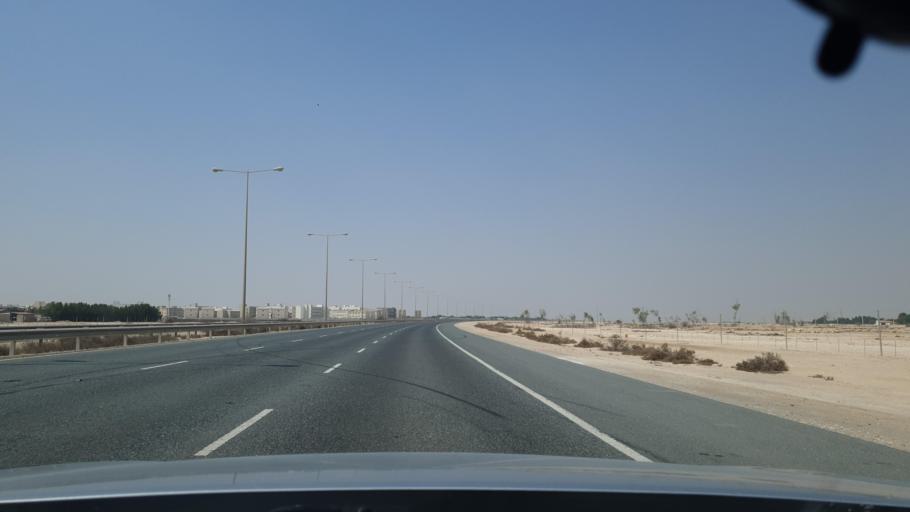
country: QA
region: Al Khawr
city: Al Khawr
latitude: 25.7560
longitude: 51.4305
